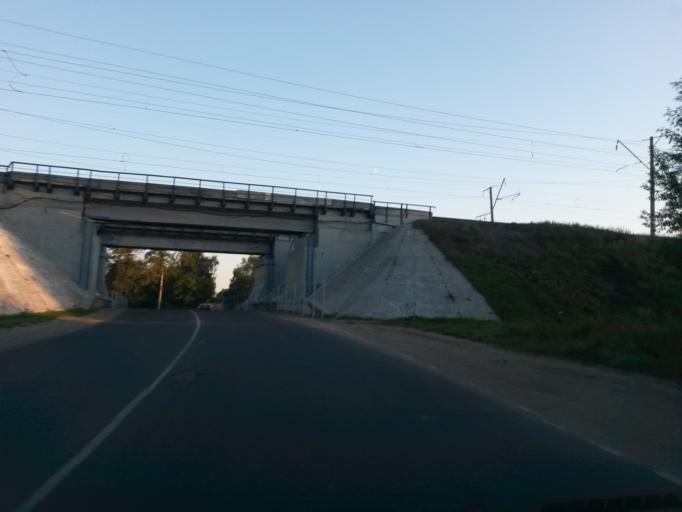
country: RU
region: Jaroslavl
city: Yaroslavl
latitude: 57.6522
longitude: 39.9063
